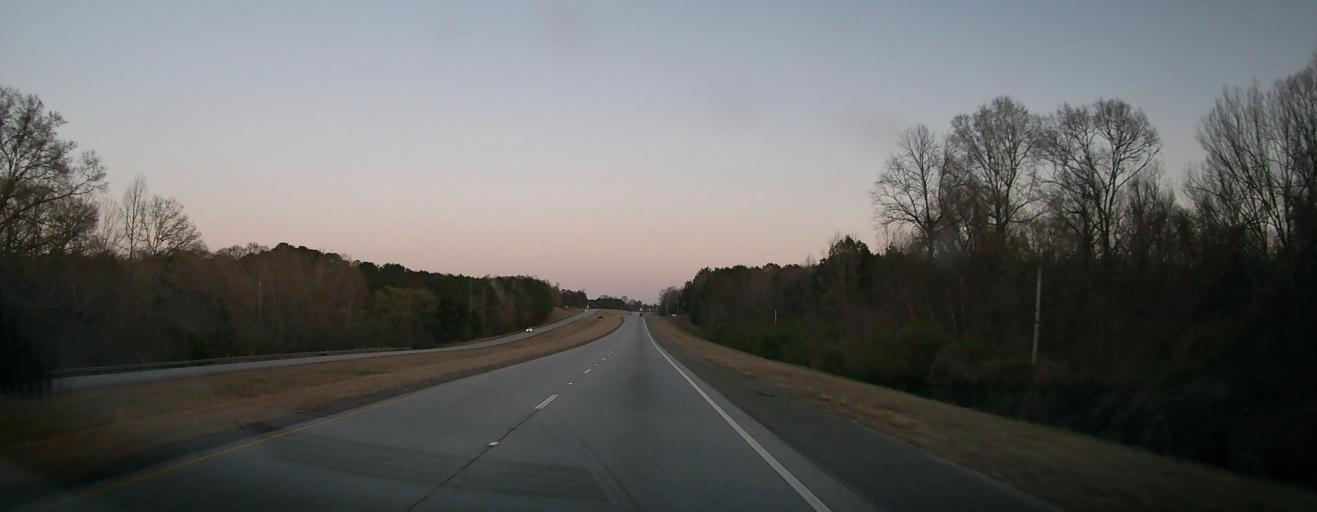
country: US
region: Alabama
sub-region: Tallapoosa County
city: Dadeville
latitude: 32.8735
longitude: -85.8098
